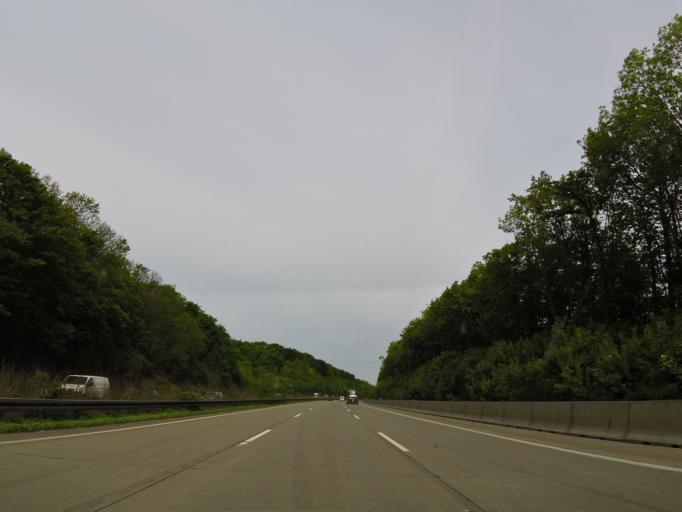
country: DE
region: Lower Saxony
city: Hildesheim
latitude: 52.1359
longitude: 10.0172
